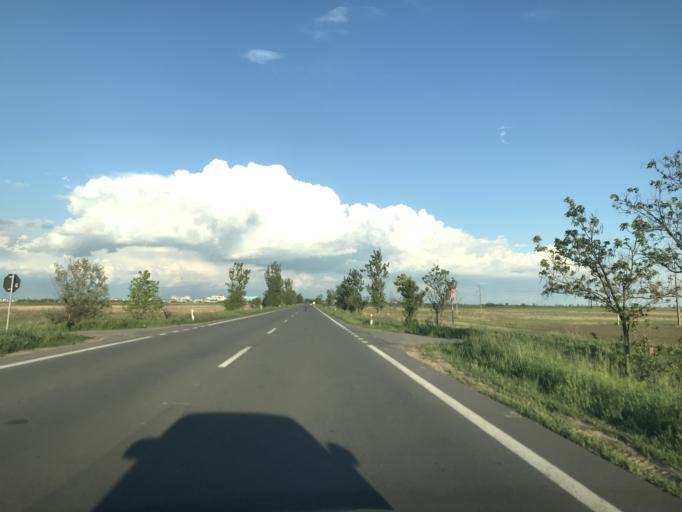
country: RS
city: Aradac
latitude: 45.3852
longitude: 20.3226
